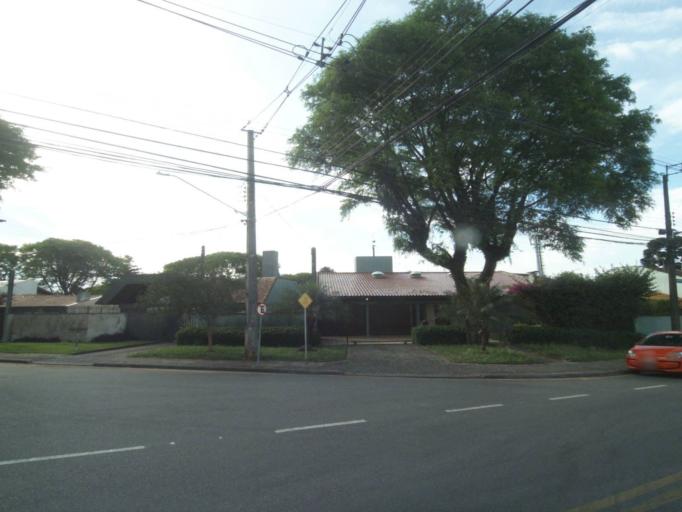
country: BR
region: Parana
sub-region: Pinhais
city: Pinhais
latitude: -25.4302
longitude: -49.2307
